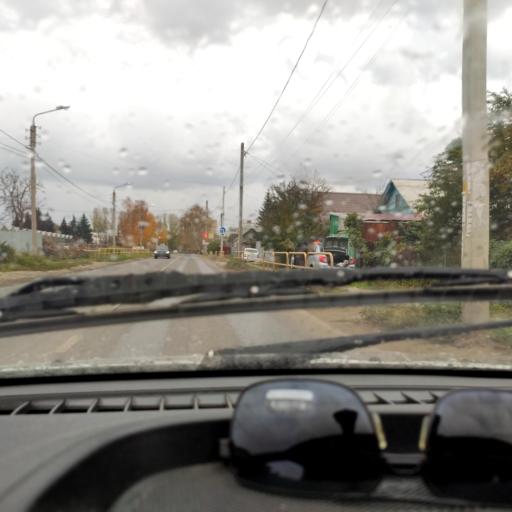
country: RU
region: Samara
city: Tol'yatti
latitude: 53.5361
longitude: 49.4284
